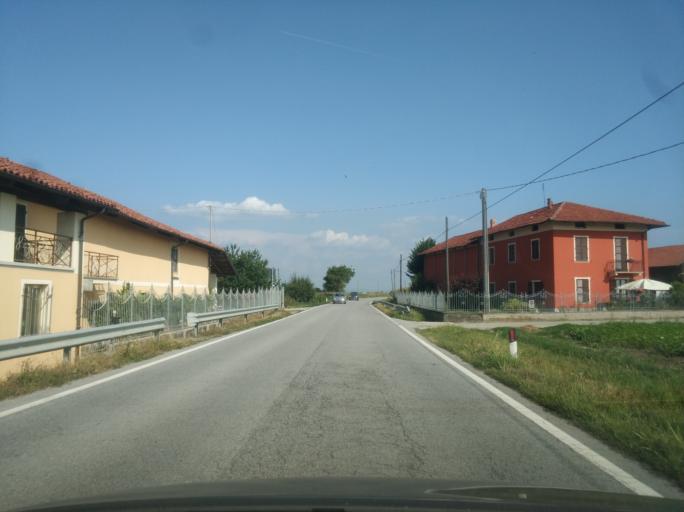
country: IT
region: Piedmont
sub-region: Provincia di Cuneo
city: Centallo
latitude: 44.5371
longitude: 7.6194
